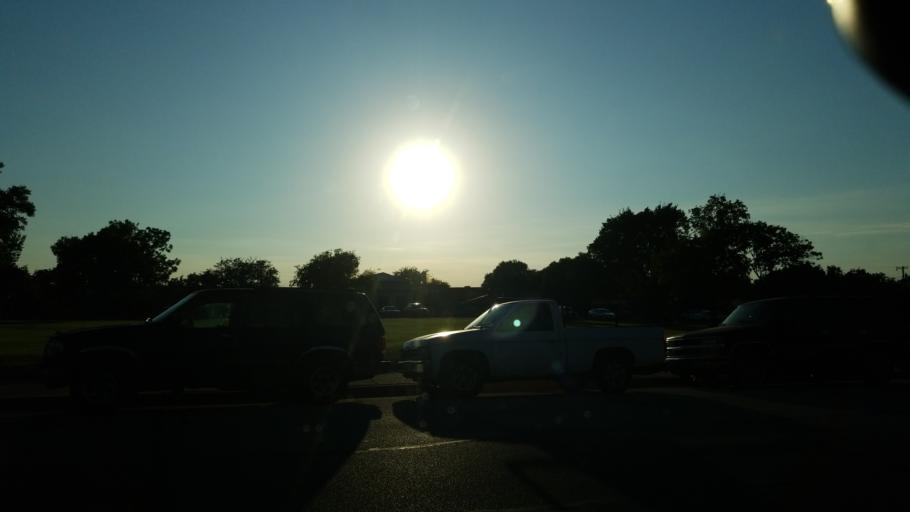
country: US
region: Texas
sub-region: Dallas County
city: Carrollton
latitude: 32.9471
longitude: -96.8976
